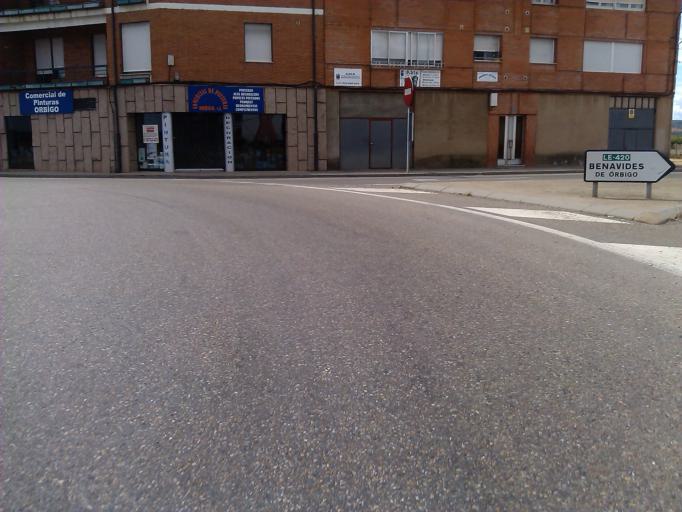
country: ES
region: Castille and Leon
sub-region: Provincia de Leon
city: Hospital de Orbigo
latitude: 42.4586
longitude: -5.8843
